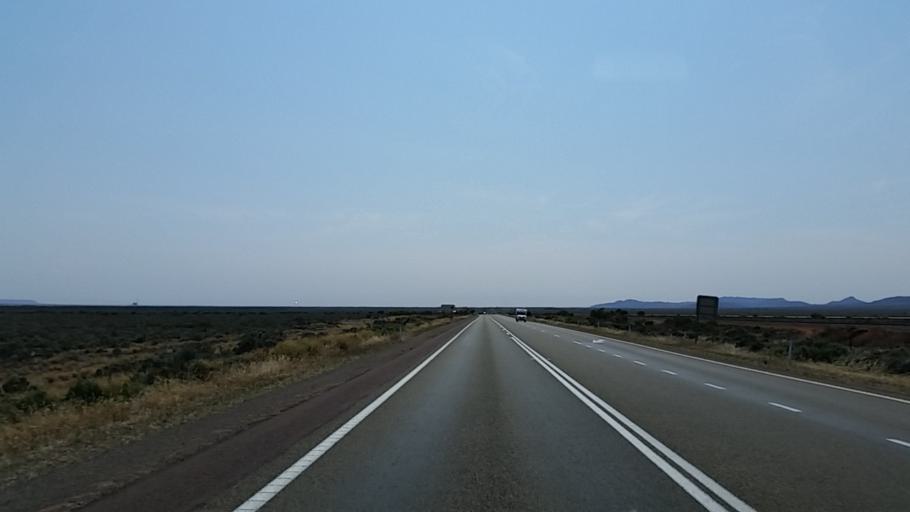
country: AU
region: South Australia
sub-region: Port Augusta
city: Port Augusta
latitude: -32.6863
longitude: 137.9395
